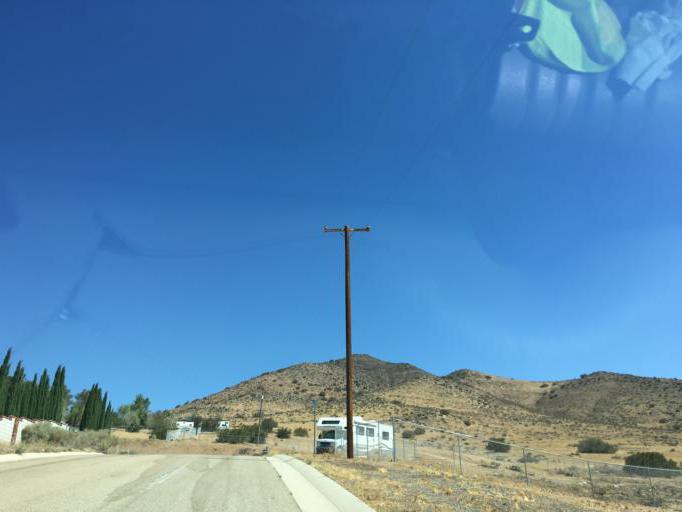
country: US
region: California
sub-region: Los Angeles County
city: Vincent
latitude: 34.4899
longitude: -118.1397
